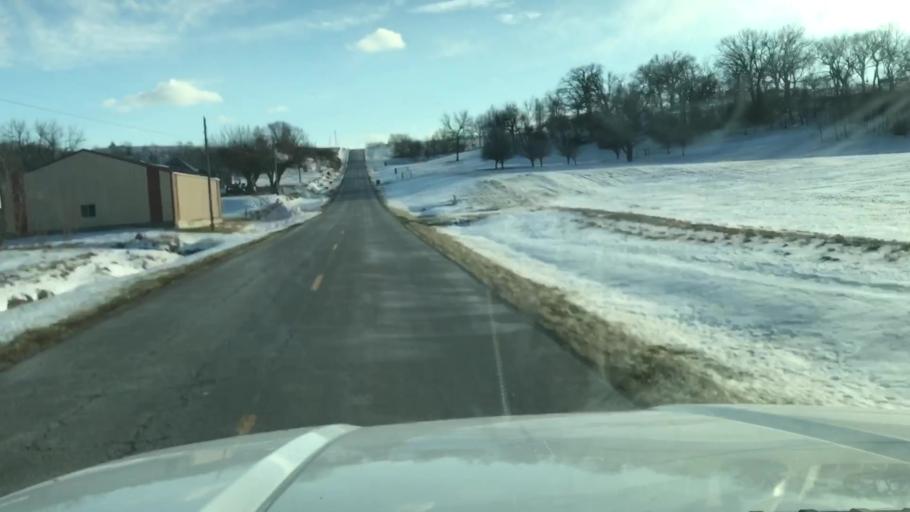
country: US
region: Missouri
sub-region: Holt County
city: Oregon
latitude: 40.0731
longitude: -94.9747
